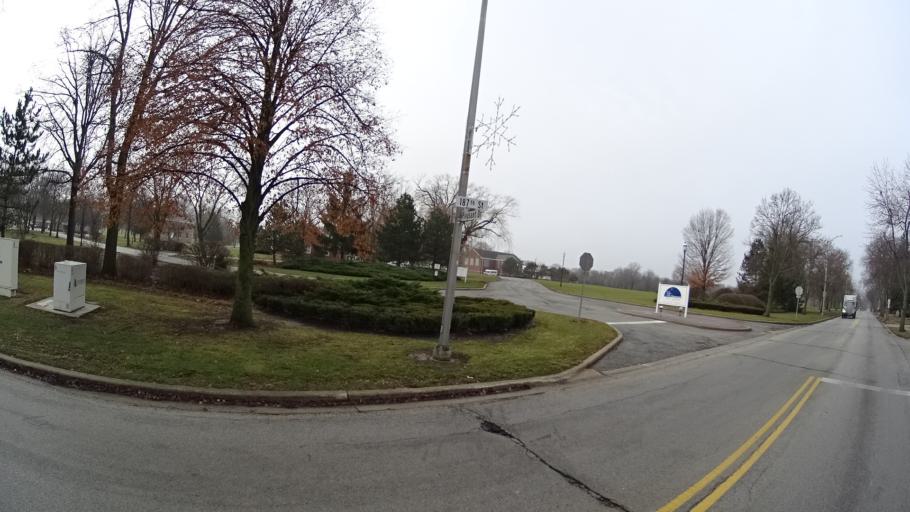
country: US
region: Illinois
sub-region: Cook County
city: Glenwood
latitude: 41.5497
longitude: -87.6295
